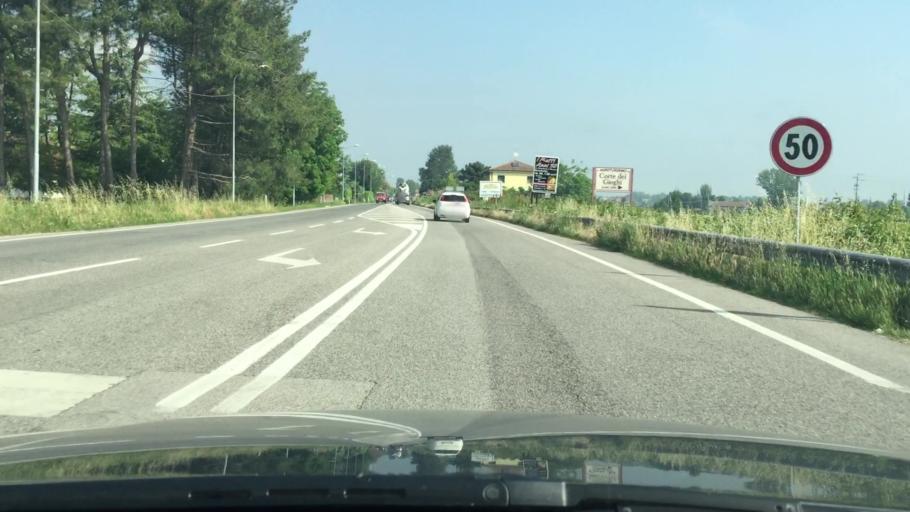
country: IT
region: Emilia-Romagna
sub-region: Provincia di Ferrara
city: Pontegradella
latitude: 44.8066
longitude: 11.6361
